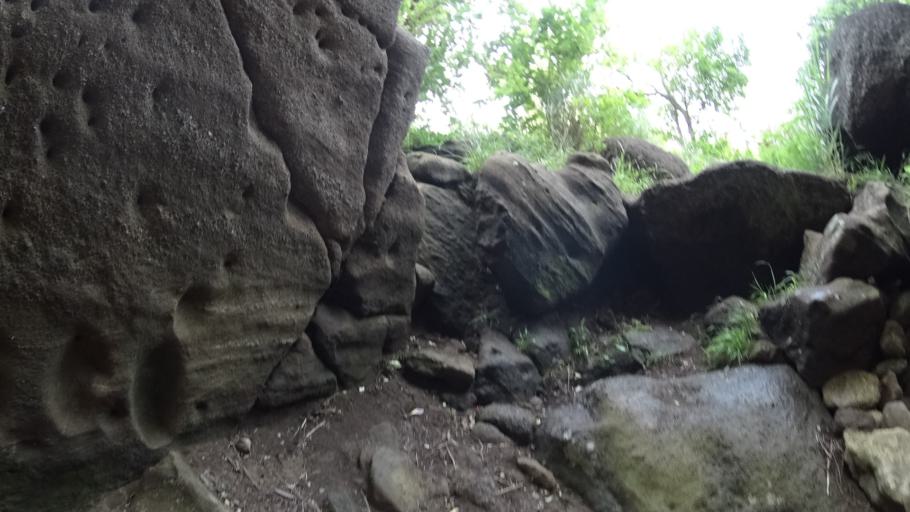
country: JP
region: Kanagawa
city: Zushi
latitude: 35.3060
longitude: 139.6142
